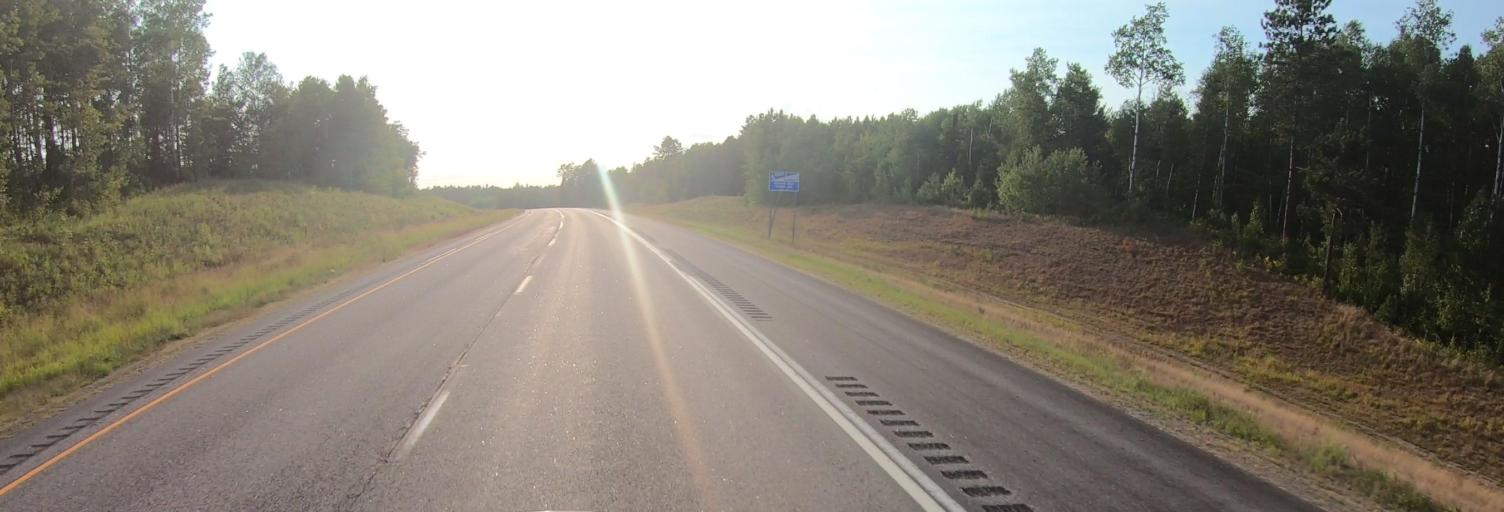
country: US
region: Minnesota
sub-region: Saint Louis County
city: Parkville
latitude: 47.6623
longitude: -92.5872
